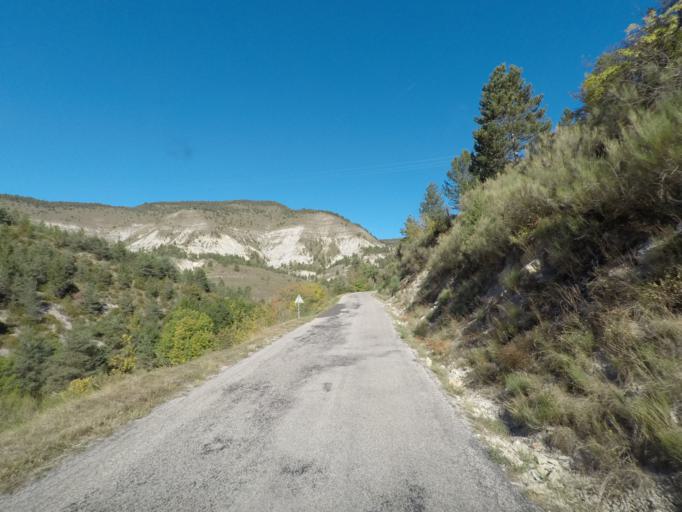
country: FR
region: Rhone-Alpes
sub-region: Departement de la Drome
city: Die
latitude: 44.5151
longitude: 5.3454
